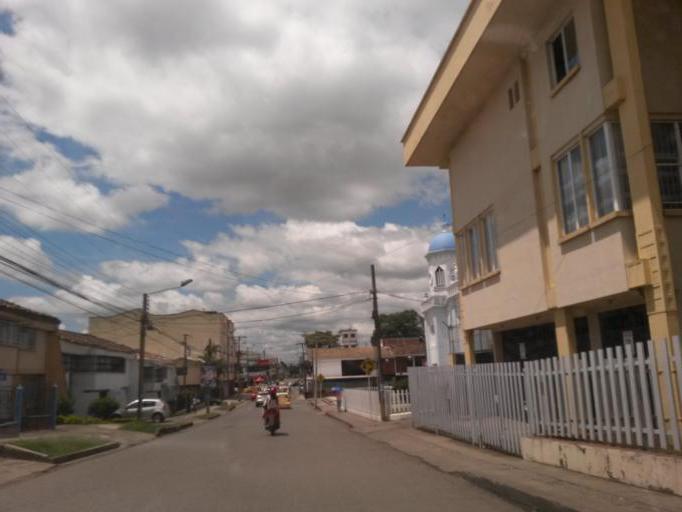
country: CO
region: Cauca
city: Popayan
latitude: 2.4507
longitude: -76.6043
